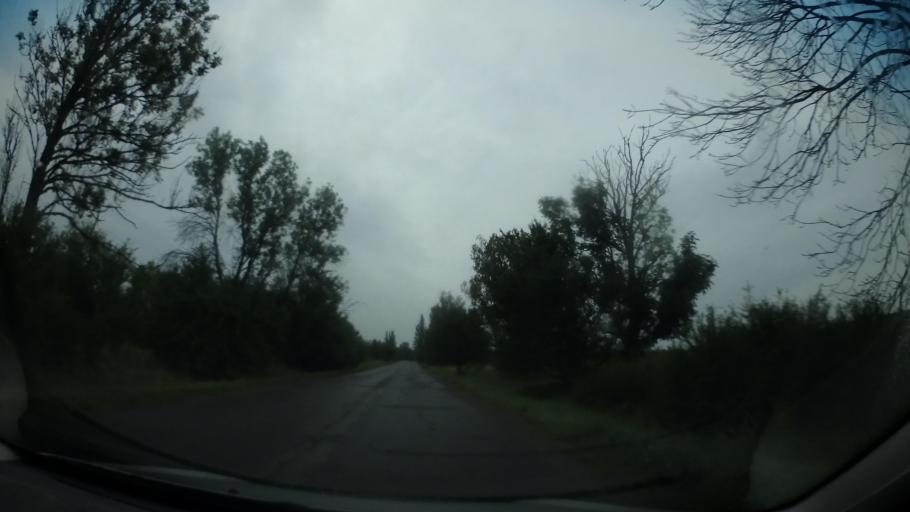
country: CZ
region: Central Bohemia
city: Milovice
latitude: 50.2375
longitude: 14.8976
